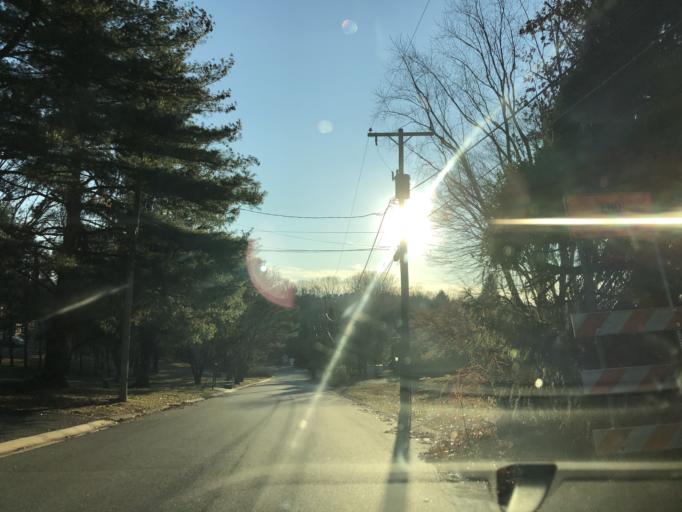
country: US
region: Pennsylvania
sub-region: Delaware County
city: Chester Heights
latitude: 39.8680
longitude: -75.4956
